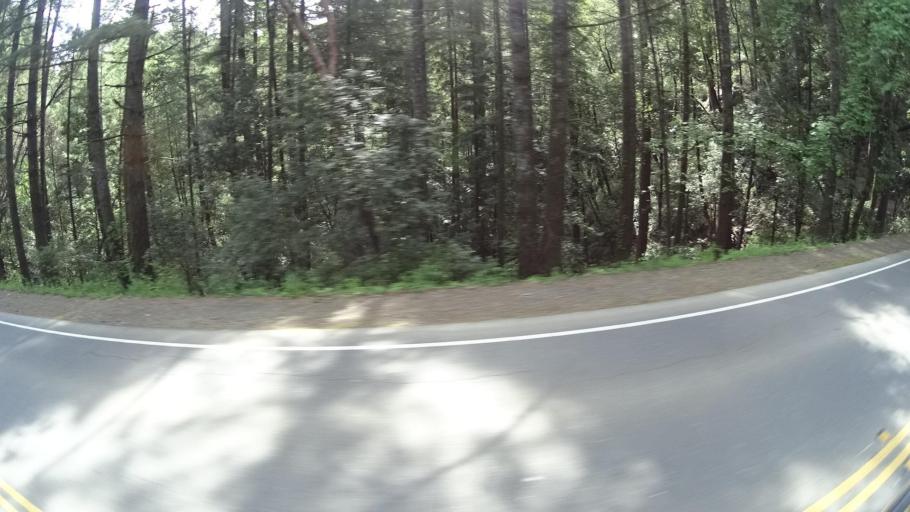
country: US
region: California
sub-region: Humboldt County
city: Redway
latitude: 40.1244
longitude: -123.8249
